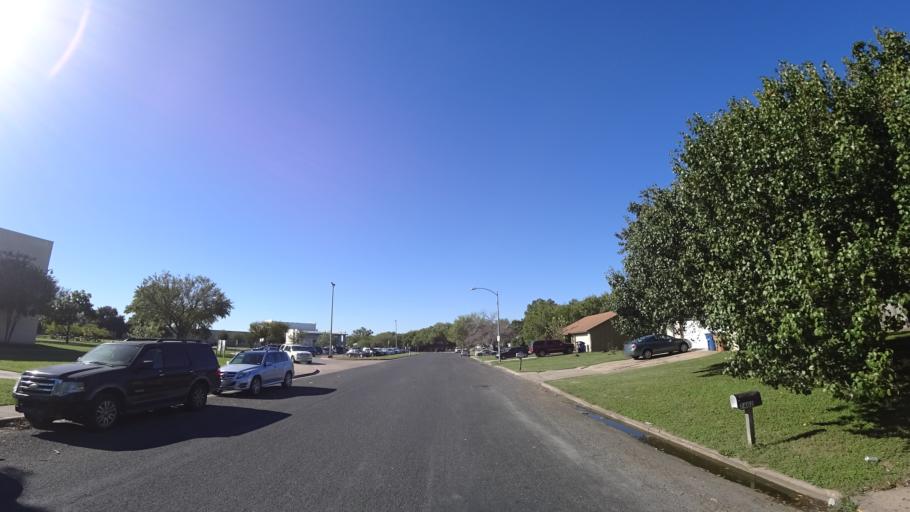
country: US
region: Texas
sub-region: Travis County
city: Austin
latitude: 30.3145
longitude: -97.6575
